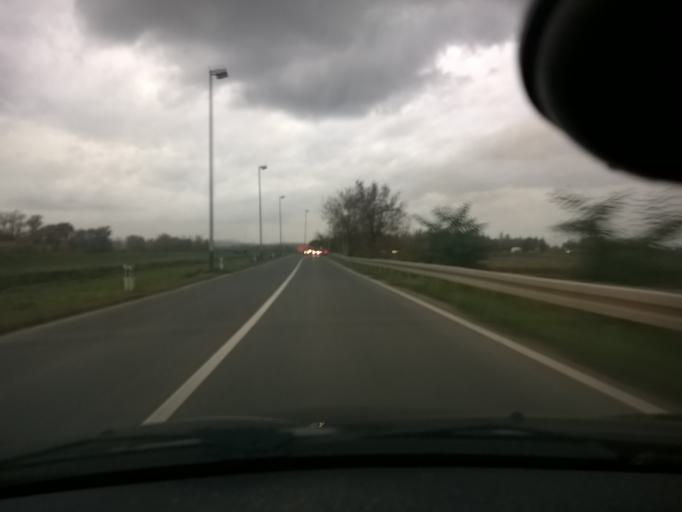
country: HR
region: Zagrebacka
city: Zapresic
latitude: 45.8450
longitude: 15.8294
